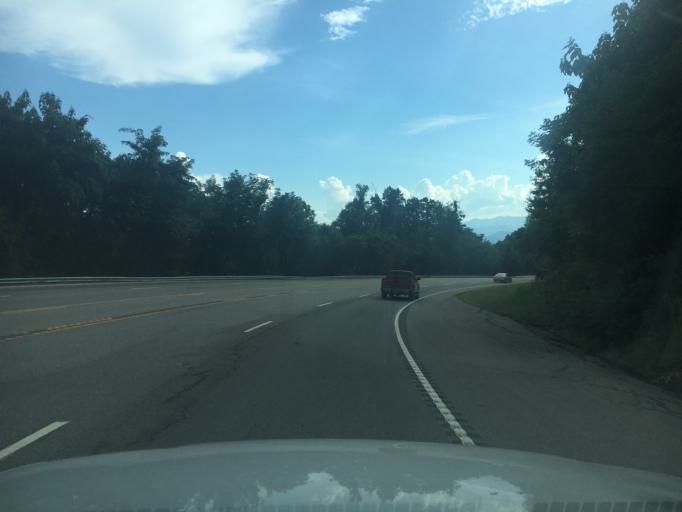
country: US
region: North Carolina
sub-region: Macon County
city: Franklin
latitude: 35.2520
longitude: -83.3161
